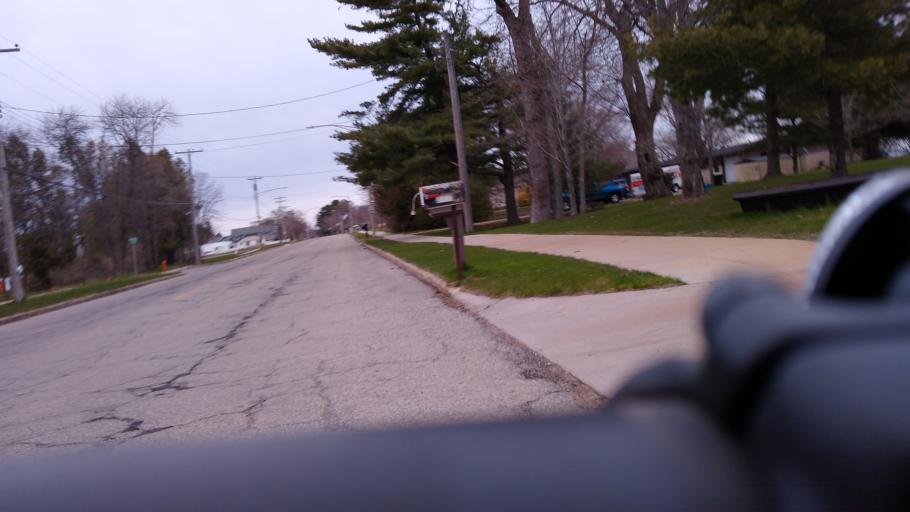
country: US
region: Michigan
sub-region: Delta County
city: Escanaba
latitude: 45.7221
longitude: -87.0694
